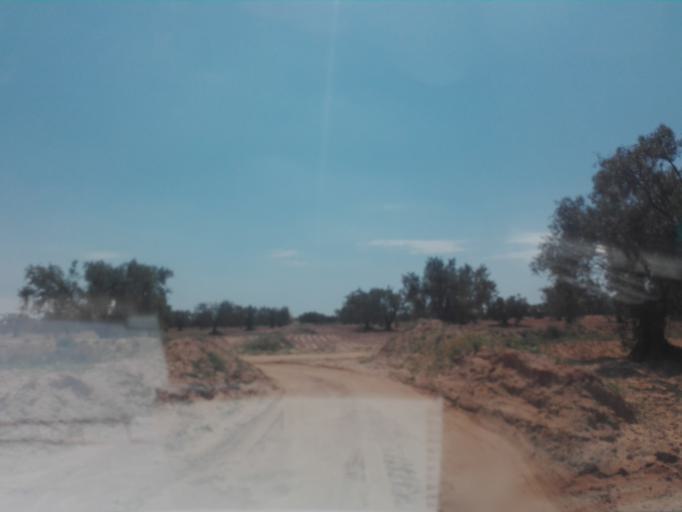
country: TN
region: Safaqis
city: Bi'r `Ali Bin Khalifah
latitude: 34.6095
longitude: 10.3540
